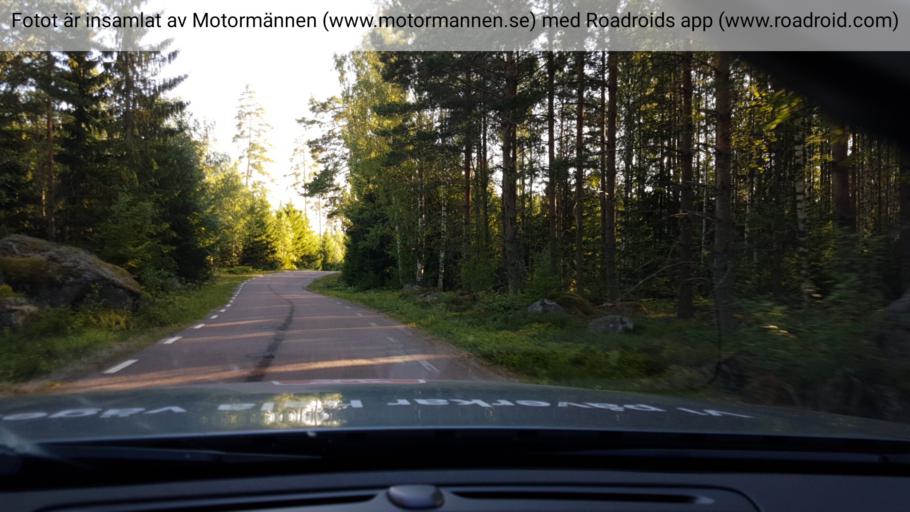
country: SE
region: Vaestmanland
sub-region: Surahammars Kommun
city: Surahammar
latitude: 59.6584
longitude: 16.0781
